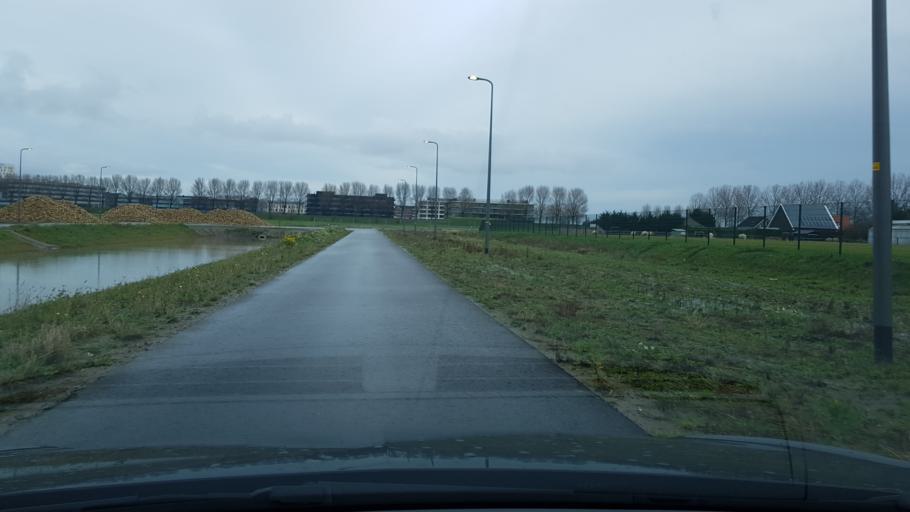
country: NL
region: North Holland
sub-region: Gemeente Haarlemmermeer
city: Hoofddorp
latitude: 52.2839
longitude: 4.6986
